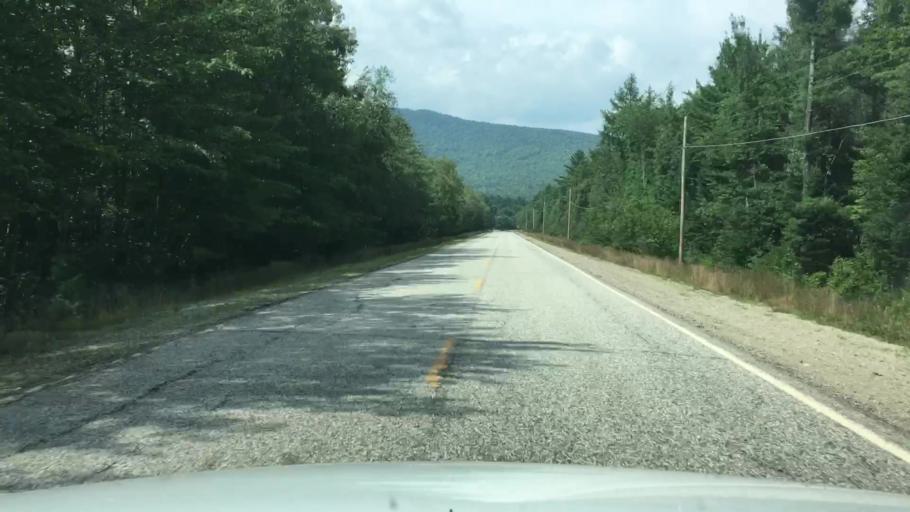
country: US
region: Maine
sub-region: Oxford County
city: Rumford
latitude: 44.5760
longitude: -70.7272
